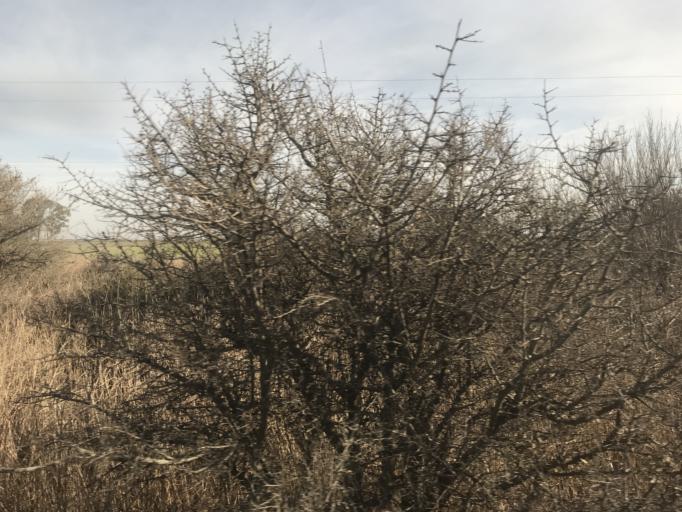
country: AR
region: Cordoba
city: Laguna Larga
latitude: -31.7614
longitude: -63.8165
